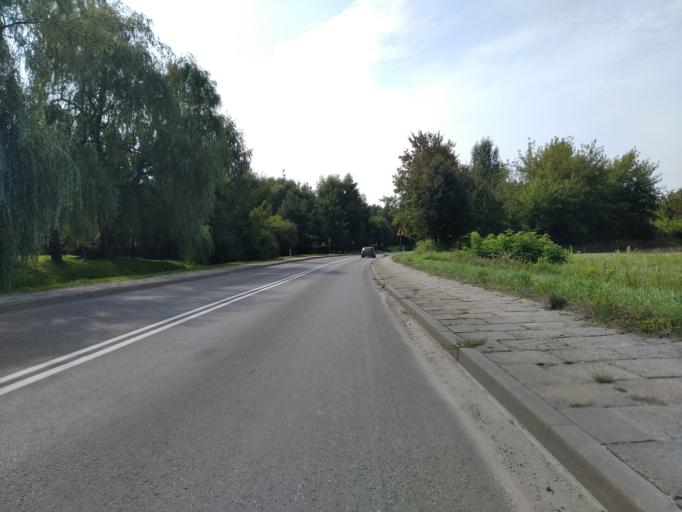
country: PL
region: Subcarpathian Voivodeship
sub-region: Powiat ropczycko-sedziszowski
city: Ostrow
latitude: 50.0863
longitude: 21.5883
